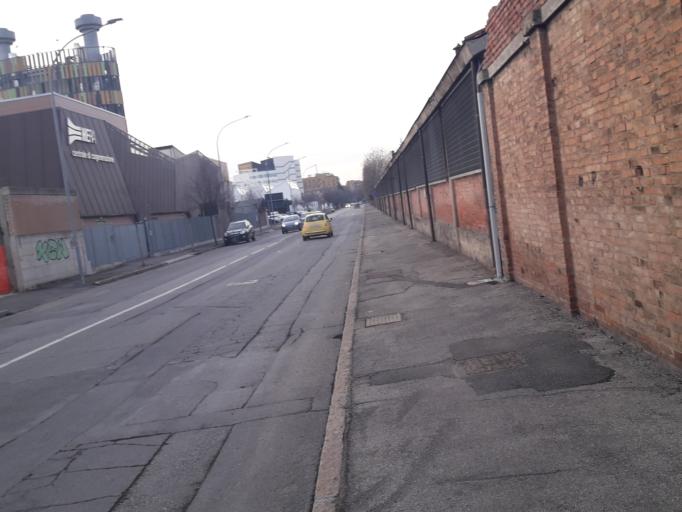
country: IT
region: Emilia-Romagna
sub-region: Provincia di Bologna
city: Bologna
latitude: 44.5081
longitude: 11.3103
